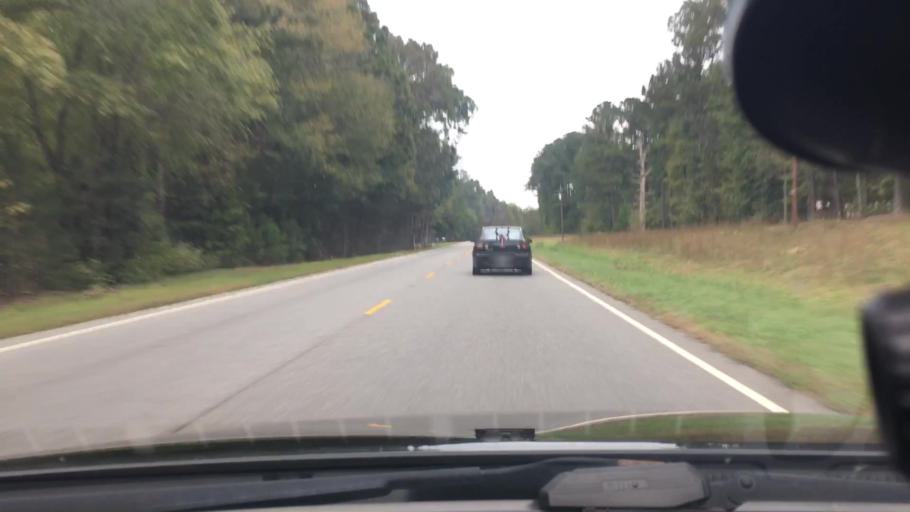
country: US
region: North Carolina
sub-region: Moore County
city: Robbins
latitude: 35.3864
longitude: -79.6529
